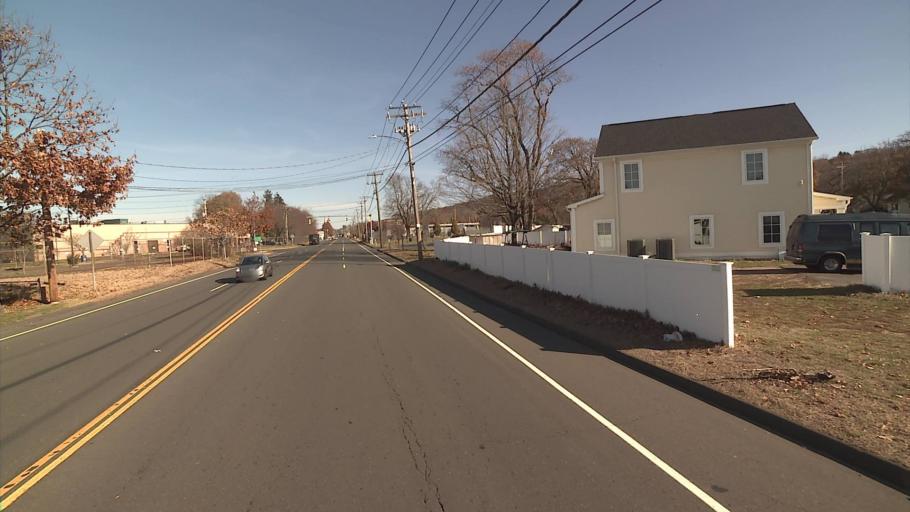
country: US
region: Connecticut
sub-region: New Haven County
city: North Haven
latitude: 41.3343
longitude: -72.8705
